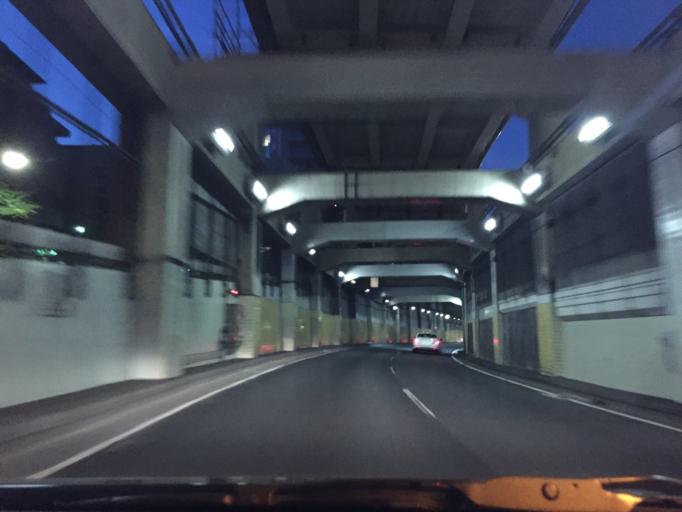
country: JP
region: Tokyo
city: Tokyo
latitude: 35.6594
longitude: 139.7367
